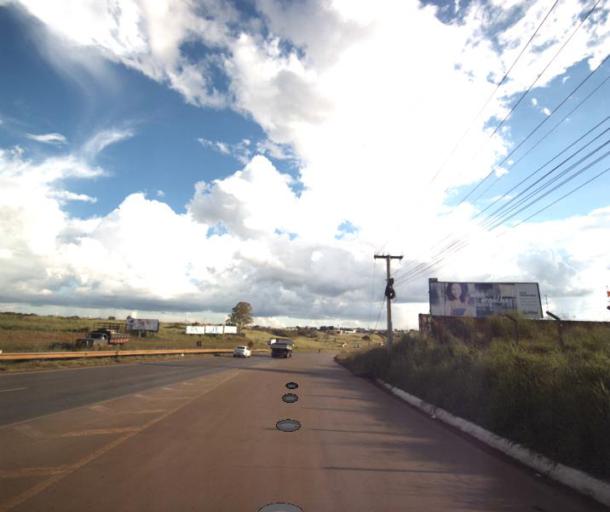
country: BR
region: Goias
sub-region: Anapolis
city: Anapolis
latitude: -16.3610
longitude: -48.9330
